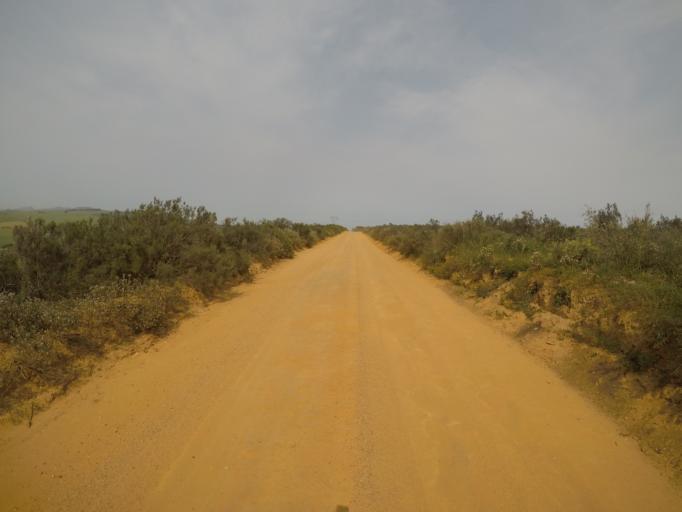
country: ZA
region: Western Cape
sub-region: West Coast District Municipality
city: Malmesbury
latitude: -33.4511
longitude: 18.7448
